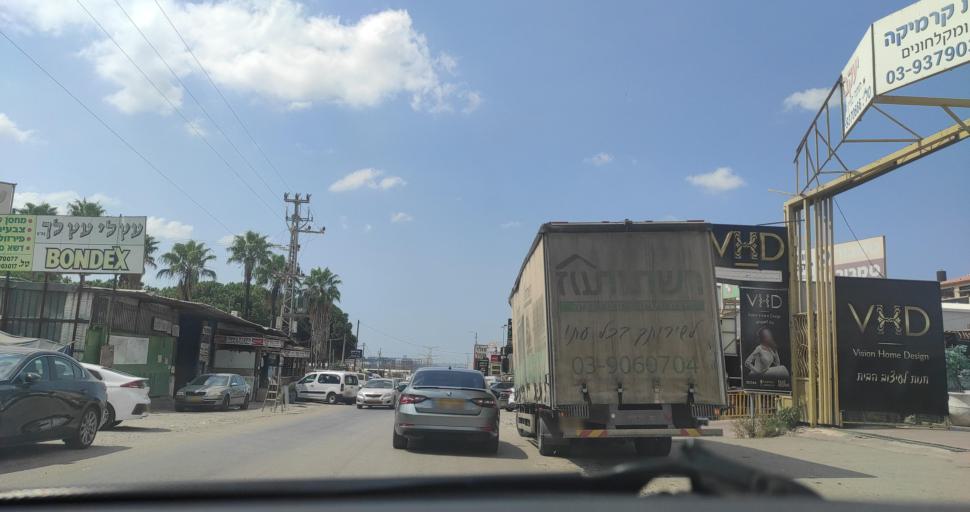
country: IL
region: Central District
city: Kafr Qasim
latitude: 32.1129
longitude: 34.9608
